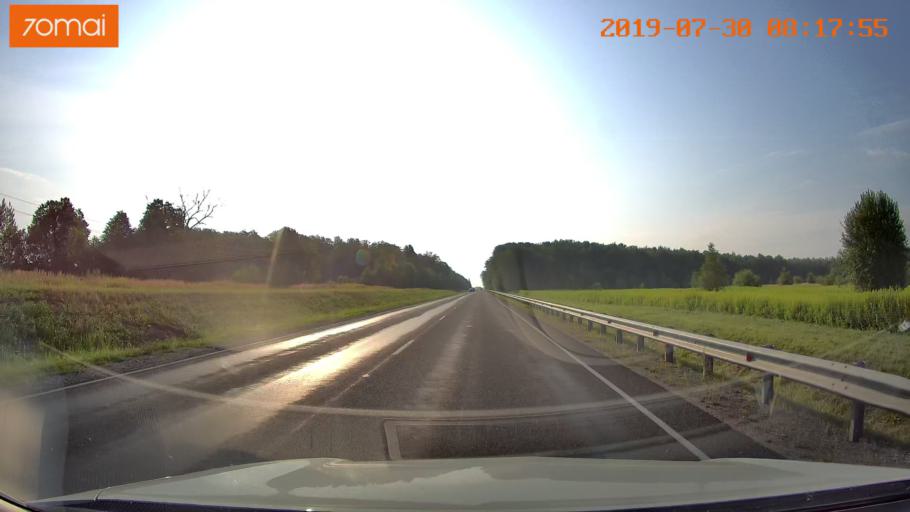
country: RU
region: Kaliningrad
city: Zheleznodorozhnyy
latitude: 54.6344
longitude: 21.4503
